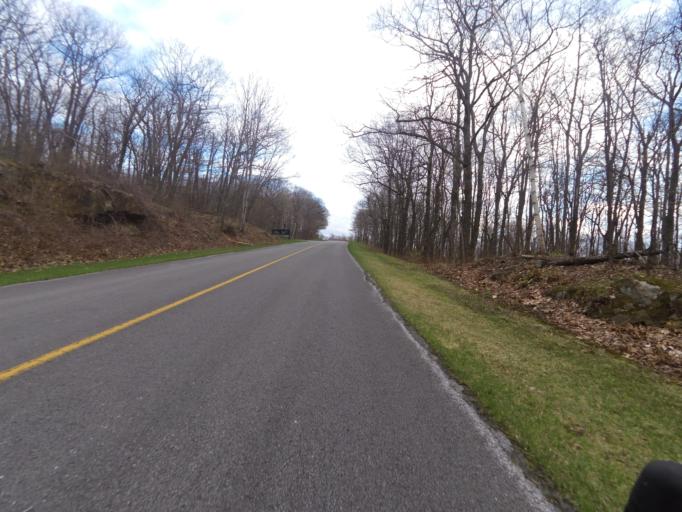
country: CA
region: Quebec
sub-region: Outaouais
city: Wakefield
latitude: 45.5059
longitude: -75.9076
